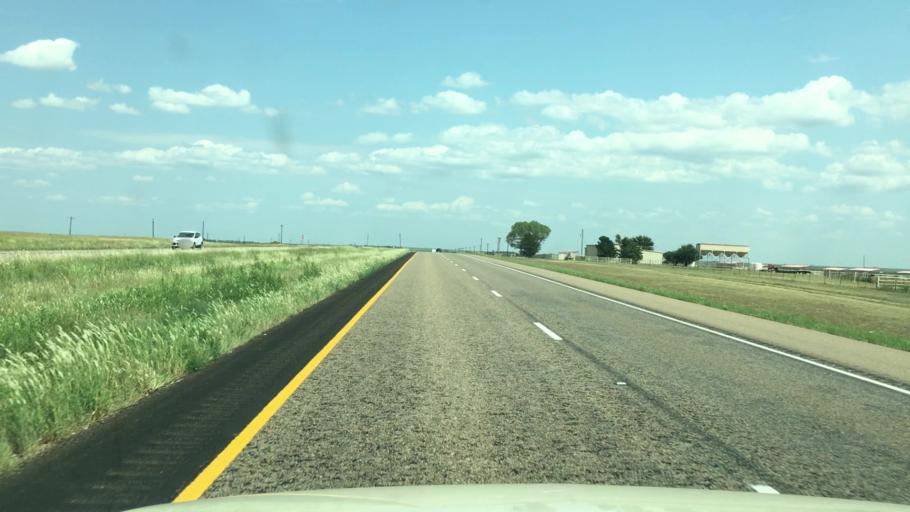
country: US
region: Texas
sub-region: Donley County
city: Clarendon
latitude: 35.0316
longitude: -101.1197
